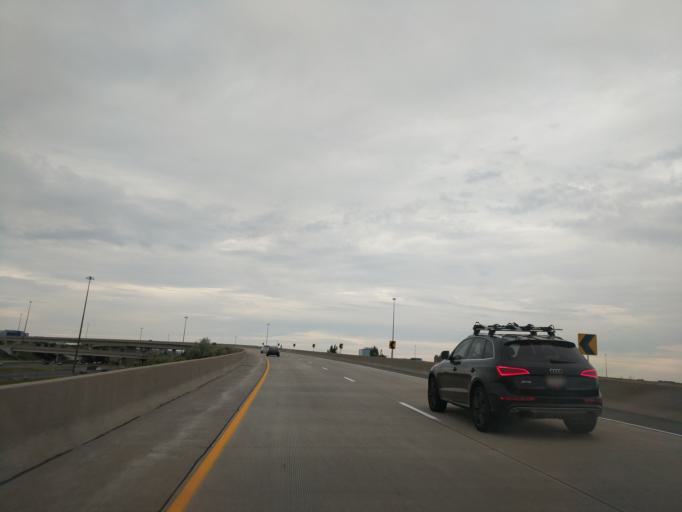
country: CA
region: Ontario
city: Willowdale
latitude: 43.8356
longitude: -79.3656
